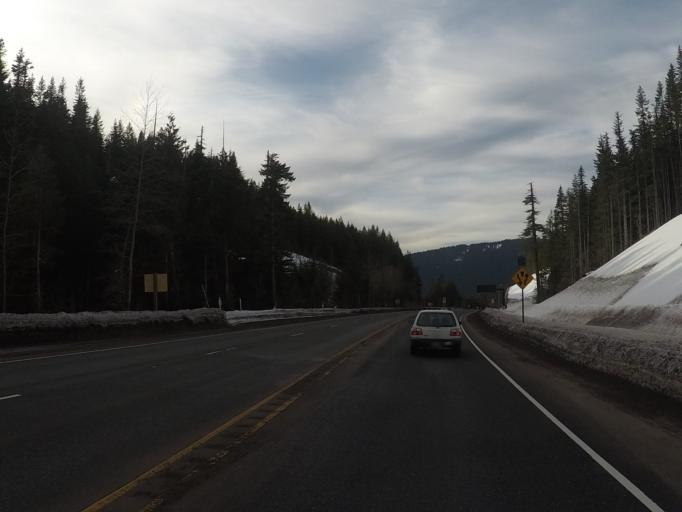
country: US
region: Oregon
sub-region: Clackamas County
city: Mount Hood Village
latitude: 45.3050
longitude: -121.7876
